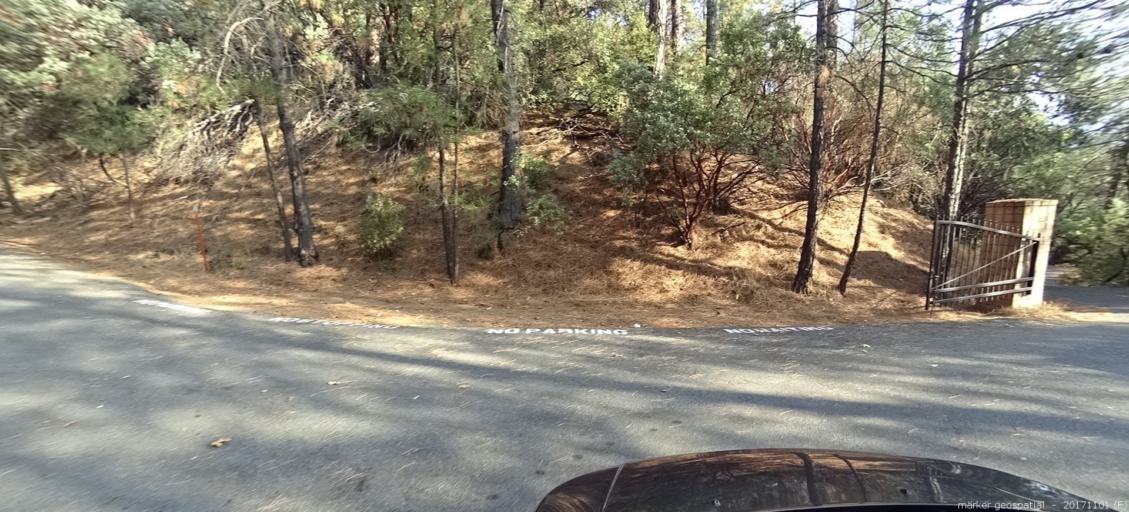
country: US
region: California
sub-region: Shasta County
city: Shasta Lake
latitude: 40.8045
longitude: -122.3045
